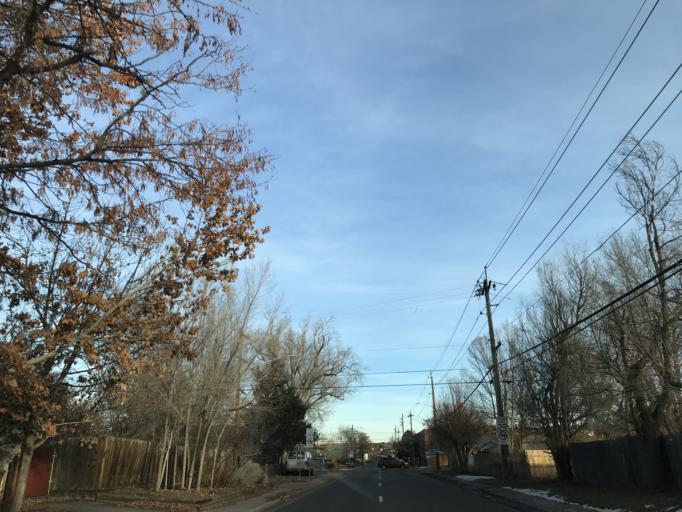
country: US
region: Colorado
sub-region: Arapahoe County
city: Glendale
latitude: 39.7387
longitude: -104.8881
